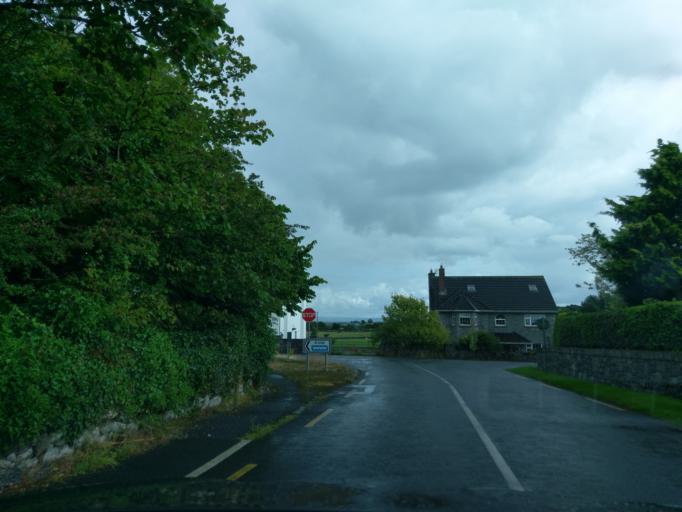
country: IE
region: Connaught
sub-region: County Galway
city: Oranmore
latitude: 53.2456
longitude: -8.9555
